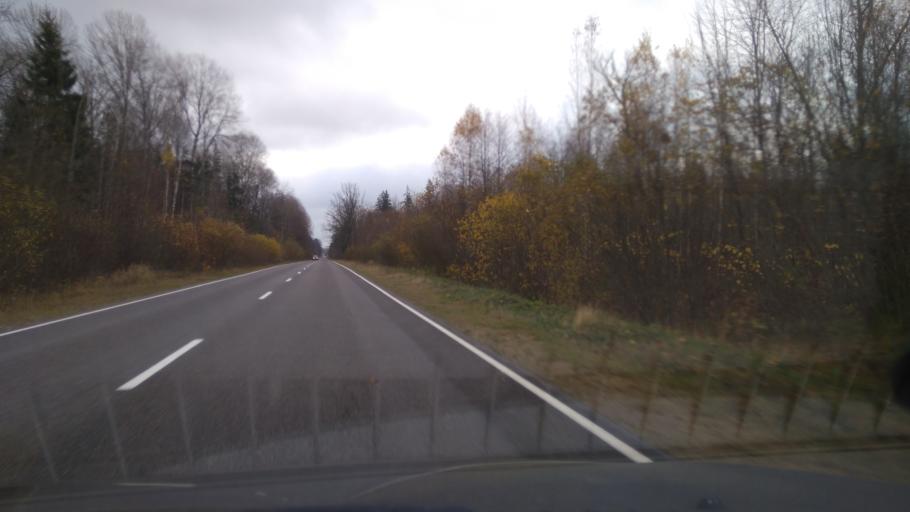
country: BY
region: Minsk
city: Urechcha
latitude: 53.2113
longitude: 27.8881
